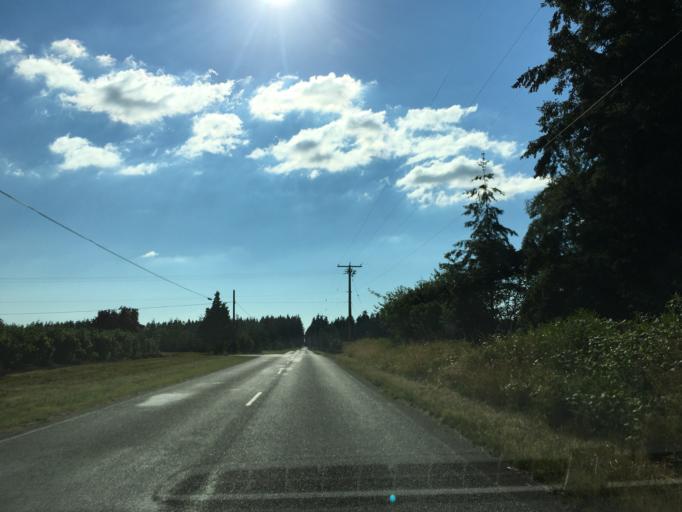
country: US
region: Washington
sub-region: Whatcom County
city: Ferndale
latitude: 48.9205
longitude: -122.5460
